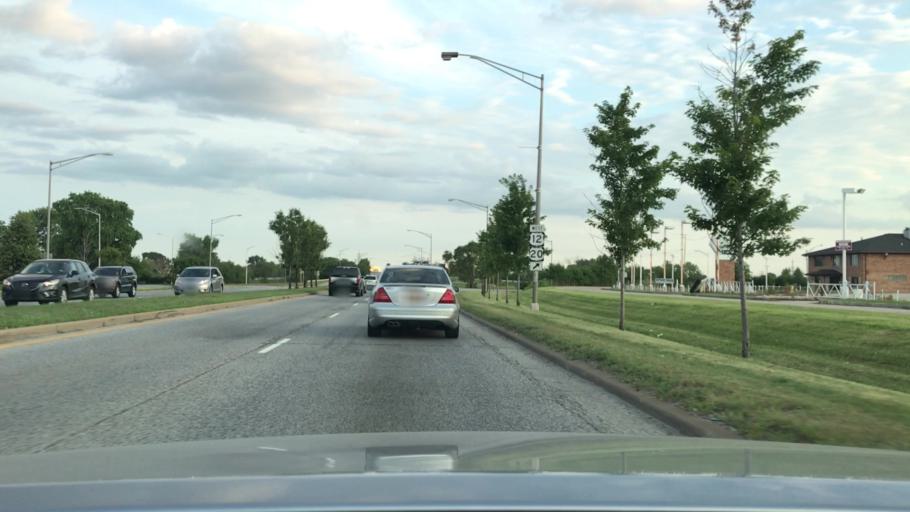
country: US
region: Illinois
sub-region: Cook County
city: Burbank
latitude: 41.7223
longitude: -87.7988
